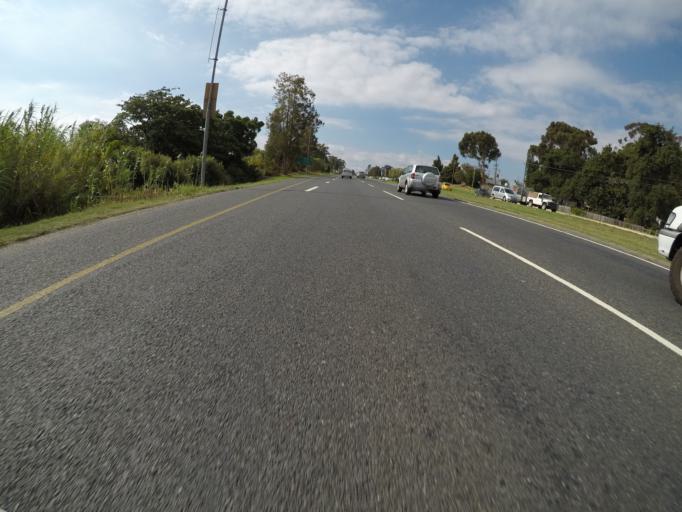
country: ZA
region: Western Cape
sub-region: Cape Winelands District Municipality
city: Stellenbosch
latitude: -33.9713
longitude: 18.8432
